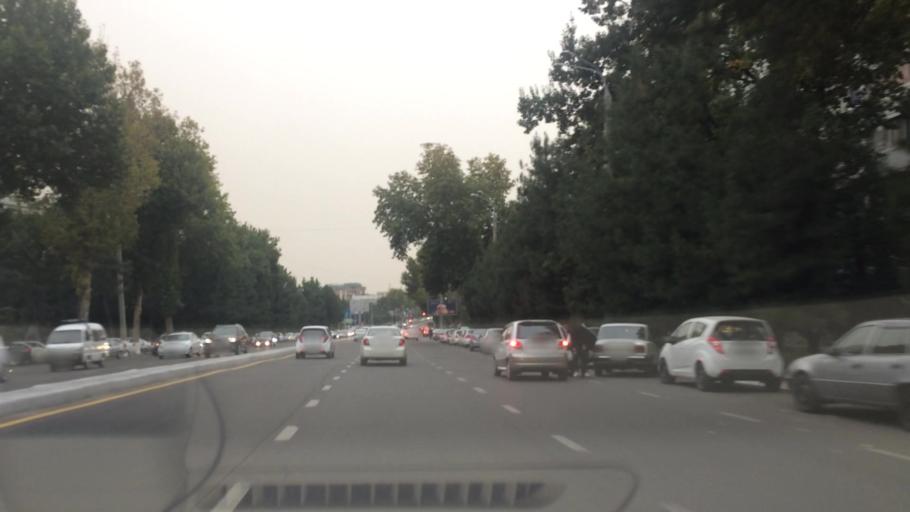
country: UZ
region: Toshkent Shahri
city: Tashkent
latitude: 41.3055
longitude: 69.2826
